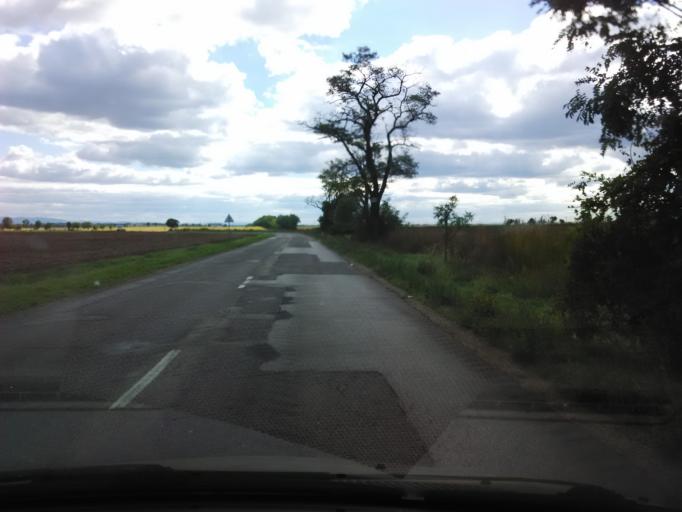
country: SK
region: Nitriansky
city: Tlmace
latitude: 48.2401
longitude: 18.4756
